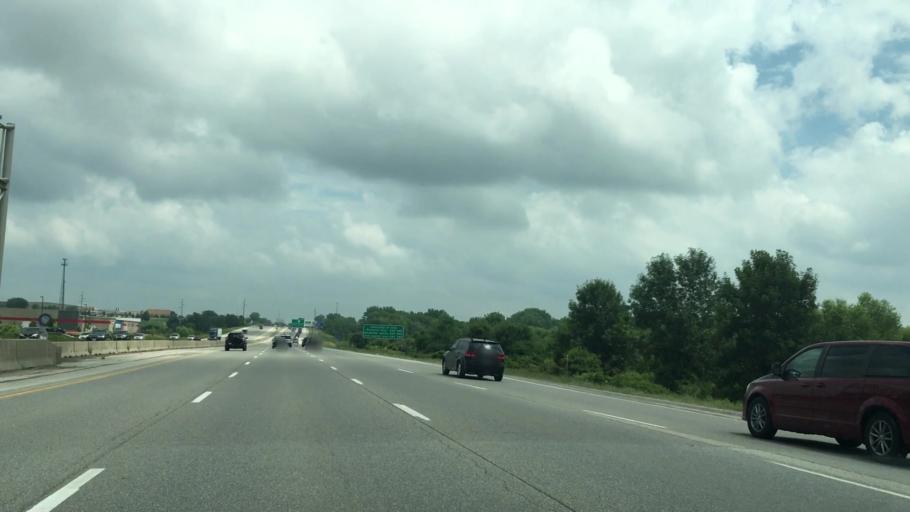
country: US
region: Iowa
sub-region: Johnson County
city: Tiffin
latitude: 41.6943
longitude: -91.6305
